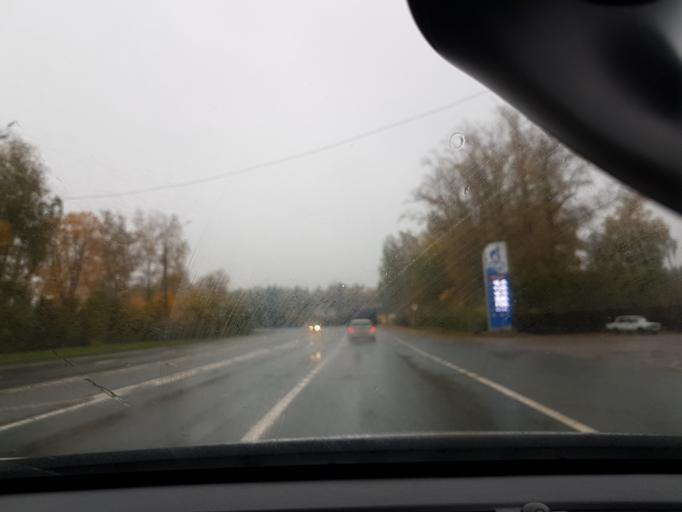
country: RU
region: Moskovskaya
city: Istra
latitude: 55.9040
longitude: 36.8970
